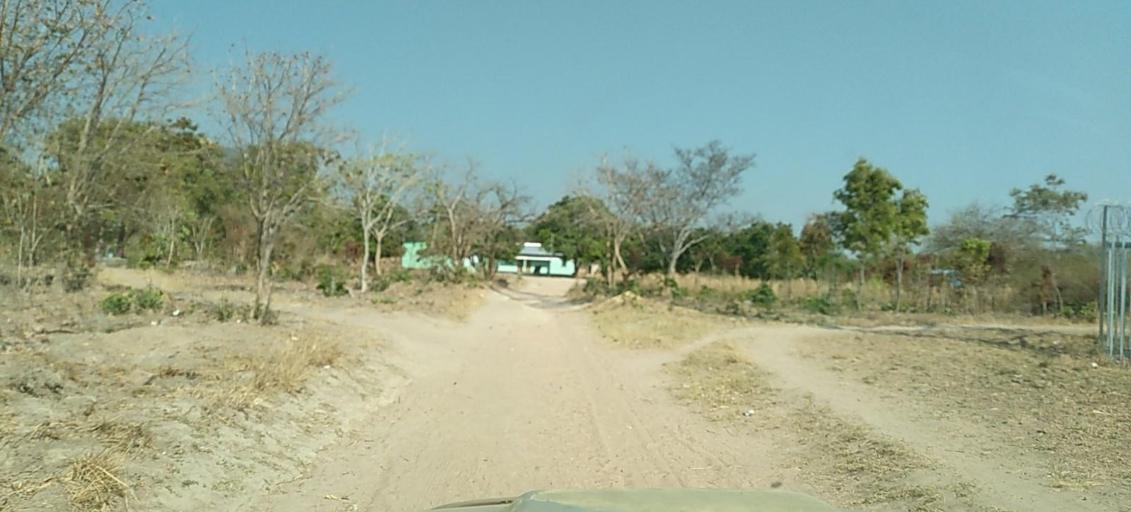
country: ZM
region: North-Western
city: Kalengwa
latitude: -13.3599
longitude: 24.8634
